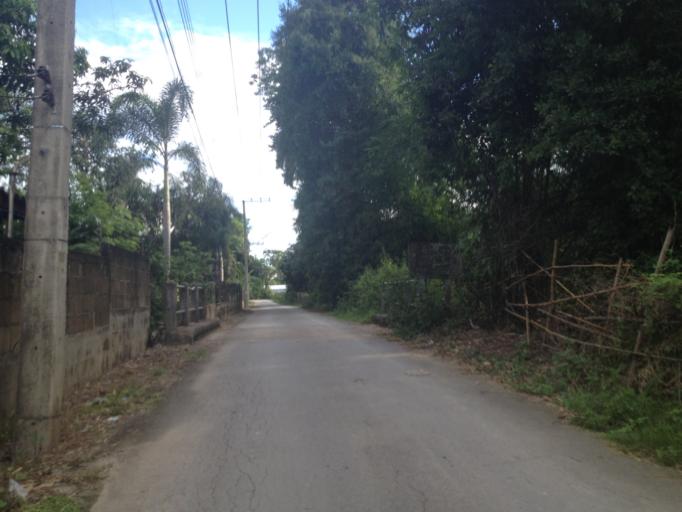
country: TH
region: Chiang Mai
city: Hang Dong
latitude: 18.6856
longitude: 98.8941
